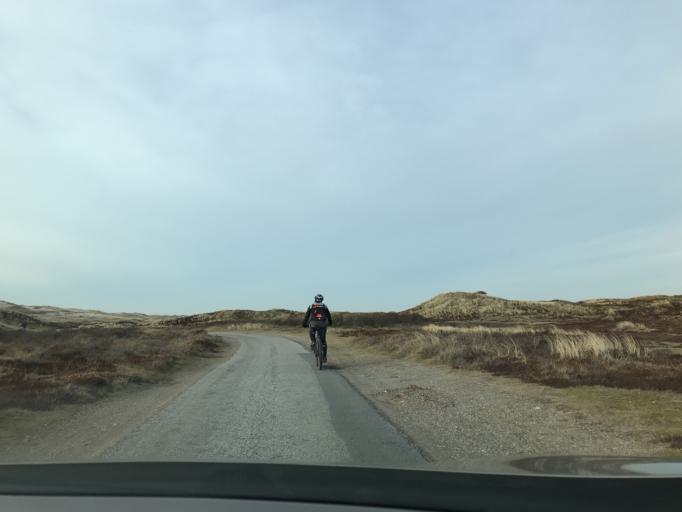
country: DK
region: Central Jutland
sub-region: Ringkobing-Skjern Kommune
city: Hvide Sande
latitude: 55.8125
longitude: 8.1774
